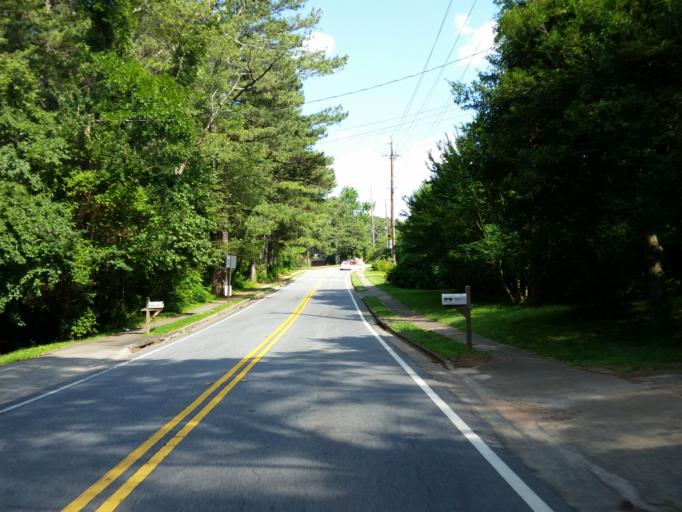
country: US
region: Georgia
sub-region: Cherokee County
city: Woodstock
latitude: 34.0276
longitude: -84.4923
